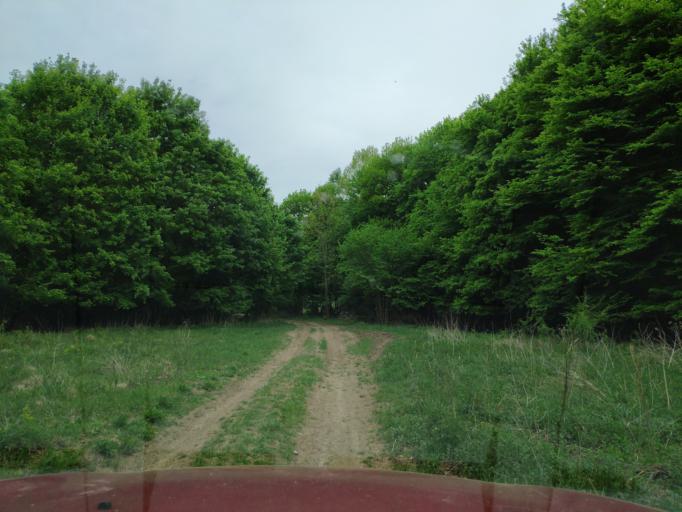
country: SK
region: Banskobystricky
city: Revuca
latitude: 48.5194
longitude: 20.1561
